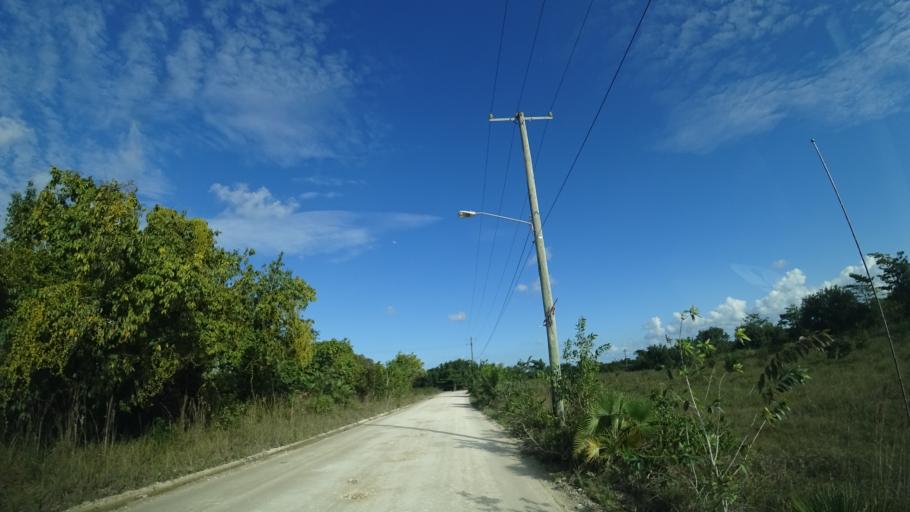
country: BZ
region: Belize
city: Belize City
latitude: 17.5566
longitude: -88.4013
